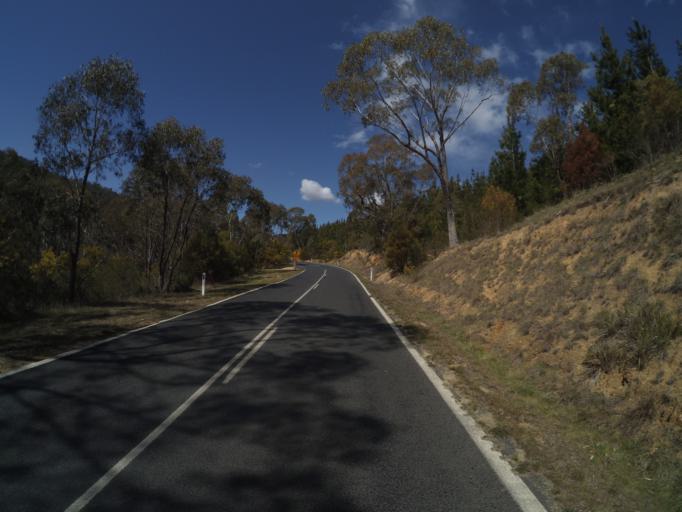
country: AU
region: Australian Capital Territory
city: Macquarie
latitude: -35.3679
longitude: 148.9596
